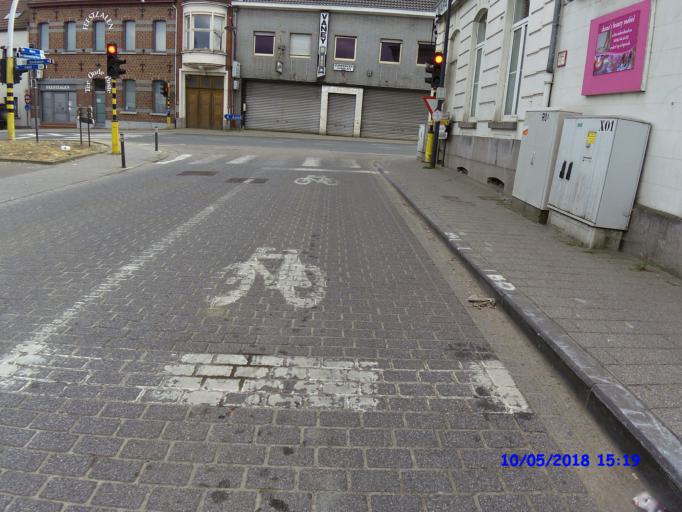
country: BE
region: Flanders
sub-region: Provincie Oost-Vlaanderen
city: Haaltert
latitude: 50.9019
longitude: 4.0067
